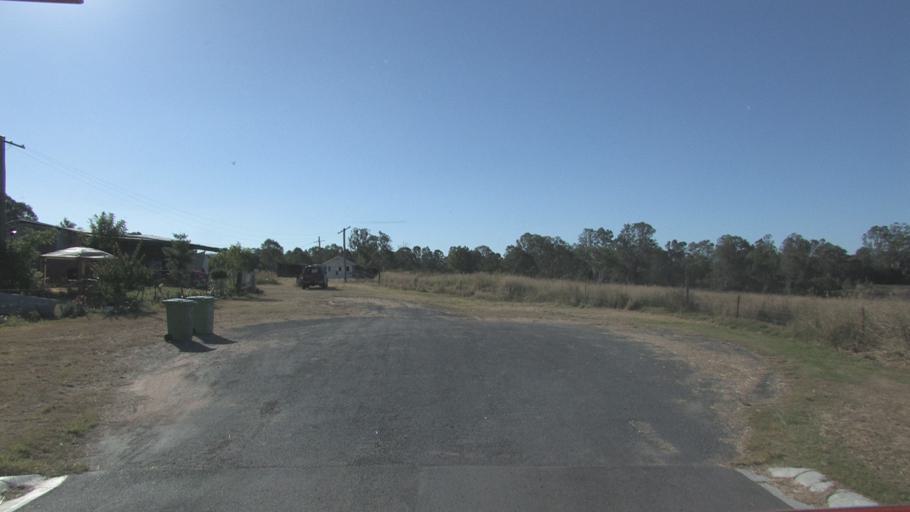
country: AU
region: Queensland
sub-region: Logan
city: North Maclean
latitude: -27.7830
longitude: 153.0253
